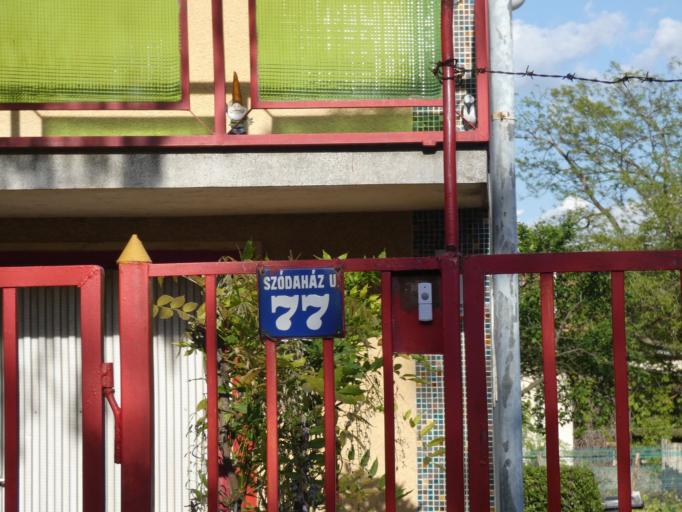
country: HU
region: Szabolcs-Szatmar-Bereg
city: Kotaj
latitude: 48.0076
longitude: 21.7312
